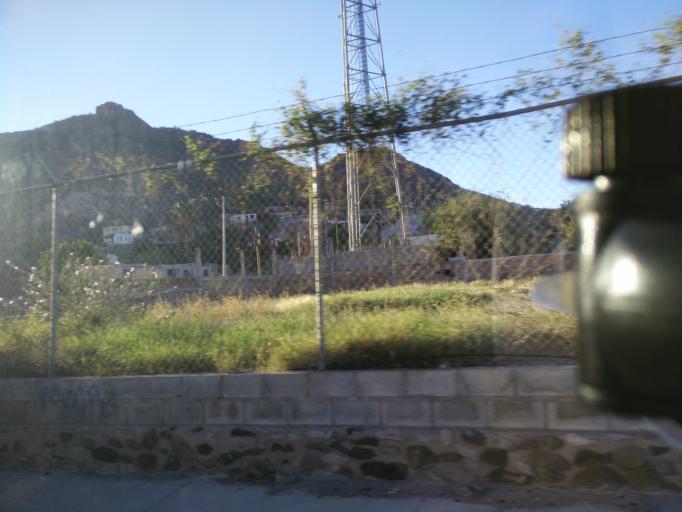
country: MX
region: Sonora
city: Heroica Guaymas
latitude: 27.9243
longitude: -110.9104
